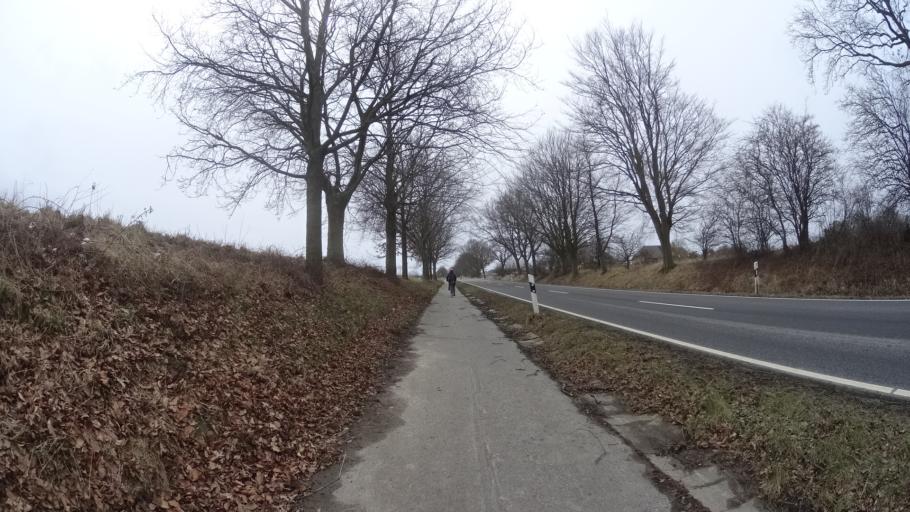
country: DE
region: Schleswig-Holstein
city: Panker
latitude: 54.3546
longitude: 10.5419
